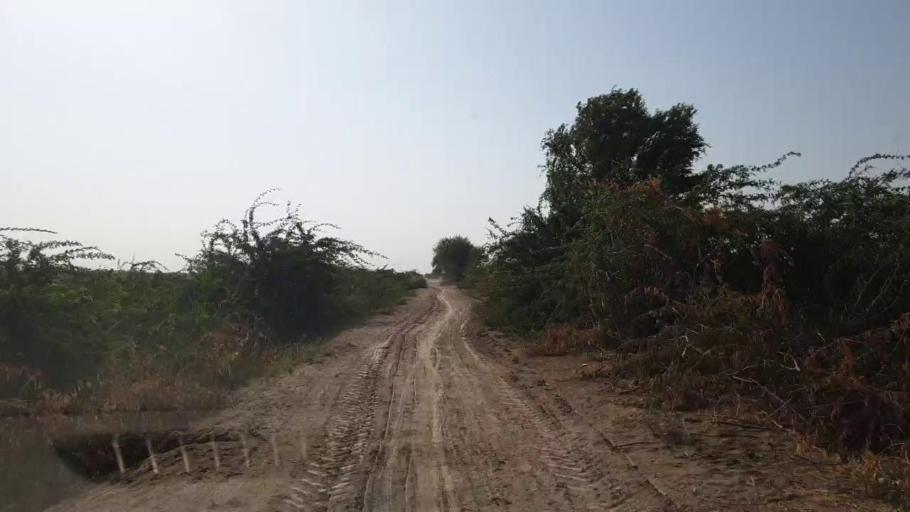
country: PK
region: Sindh
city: Kadhan
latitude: 24.5863
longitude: 69.0780
